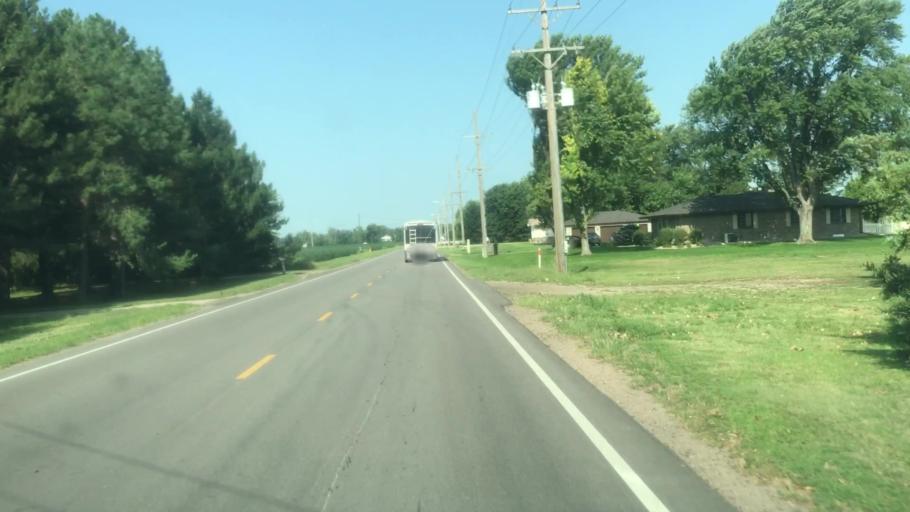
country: US
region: Nebraska
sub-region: Hall County
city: Grand Island
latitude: 40.9456
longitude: -98.3253
